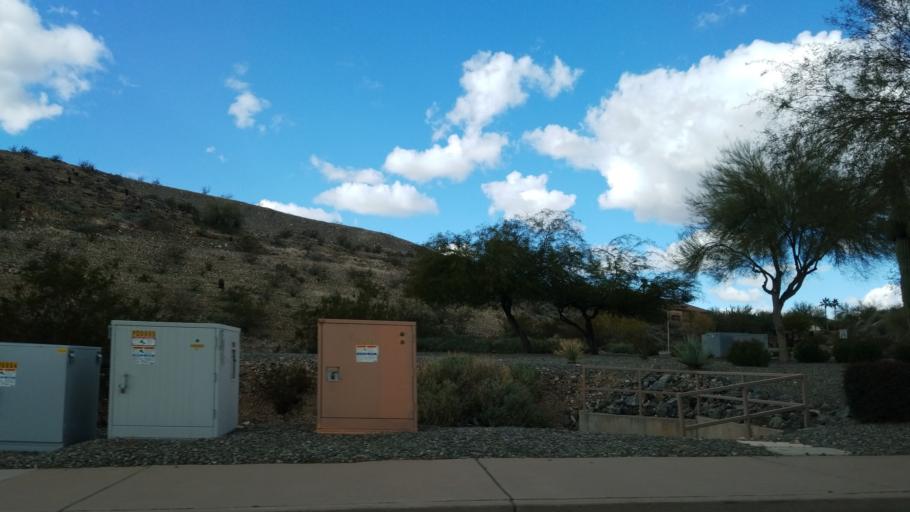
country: US
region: Arizona
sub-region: Maricopa County
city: Guadalupe
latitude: 33.2964
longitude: -112.0340
